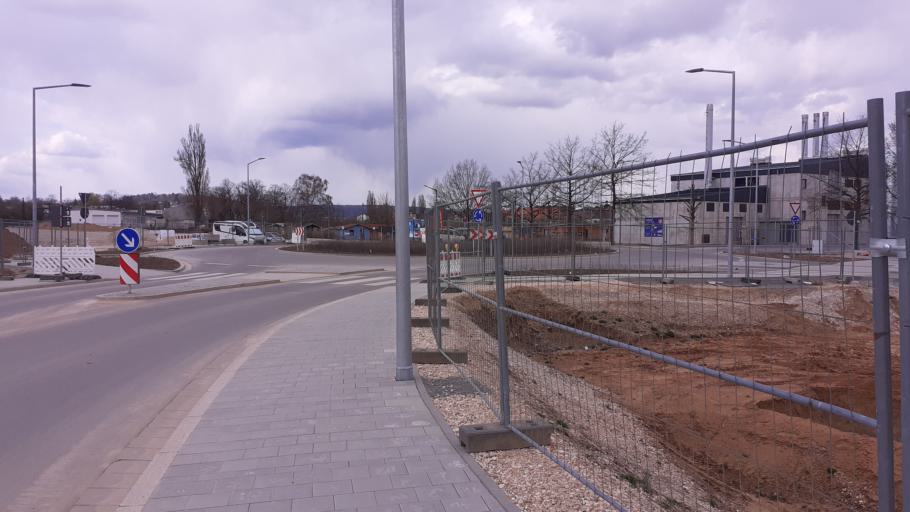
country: DE
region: Bavaria
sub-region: Upper Palatinate
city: Pentling
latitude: 49.0132
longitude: 12.0744
